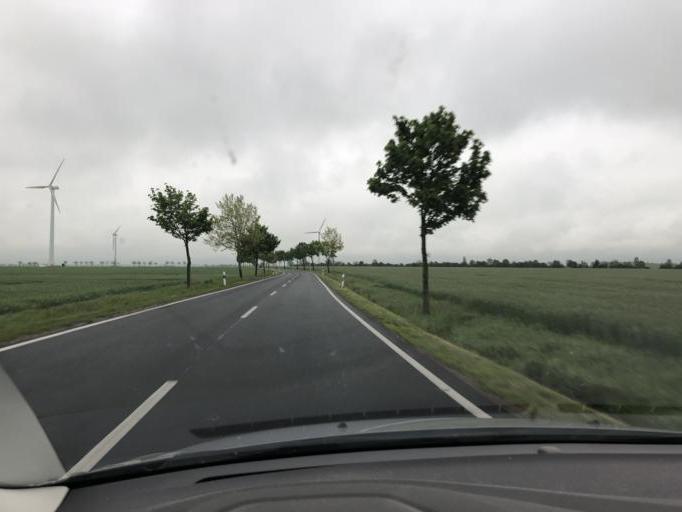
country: DE
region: Saxony
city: Dobernitz
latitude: 51.5077
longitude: 12.3772
